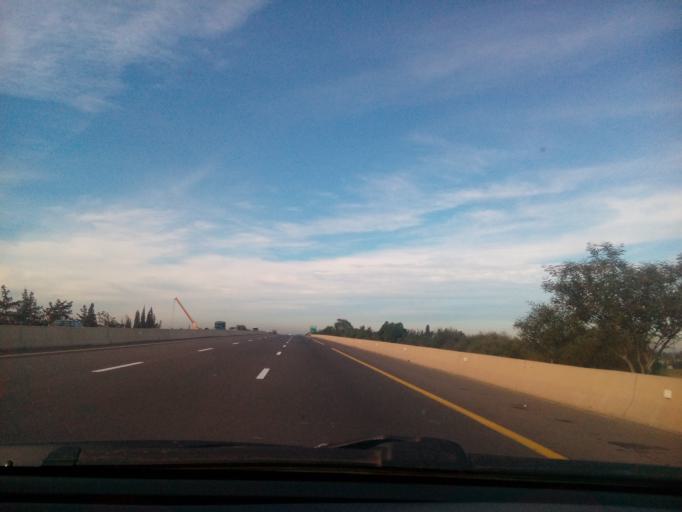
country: DZ
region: Mascara
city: Mascara
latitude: 35.6225
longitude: 0.0646
